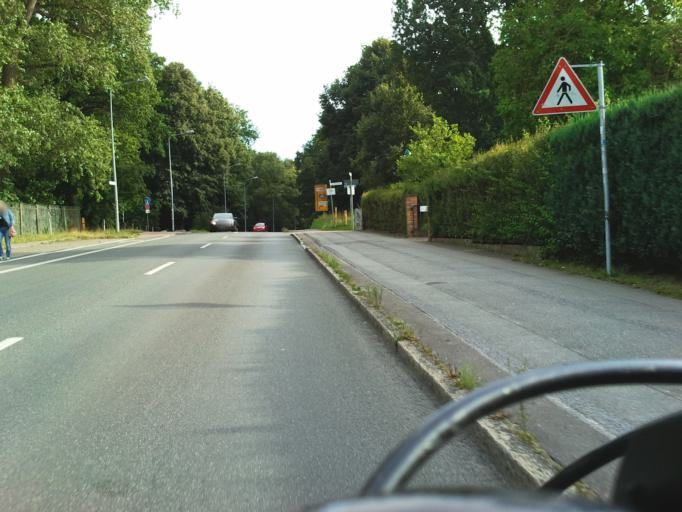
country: DE
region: Mecklenburg-Vorpommern
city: Kritzmow
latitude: 54.0833
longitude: 12.0876
